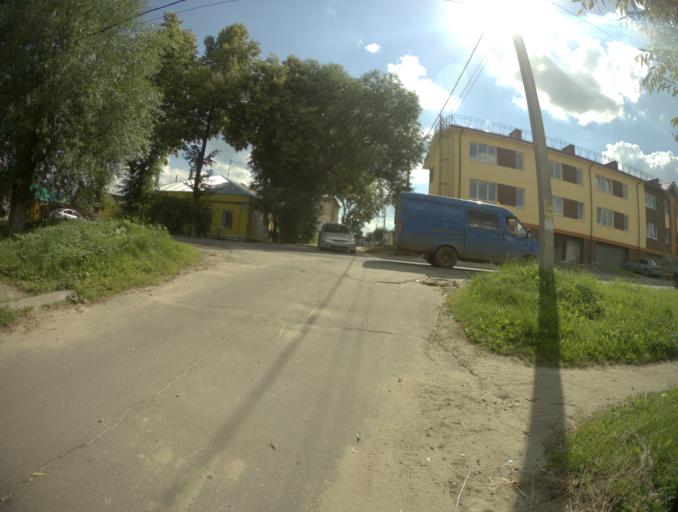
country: RU
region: Vladimir
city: Vladimir
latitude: 56.1260
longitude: 40.3771
